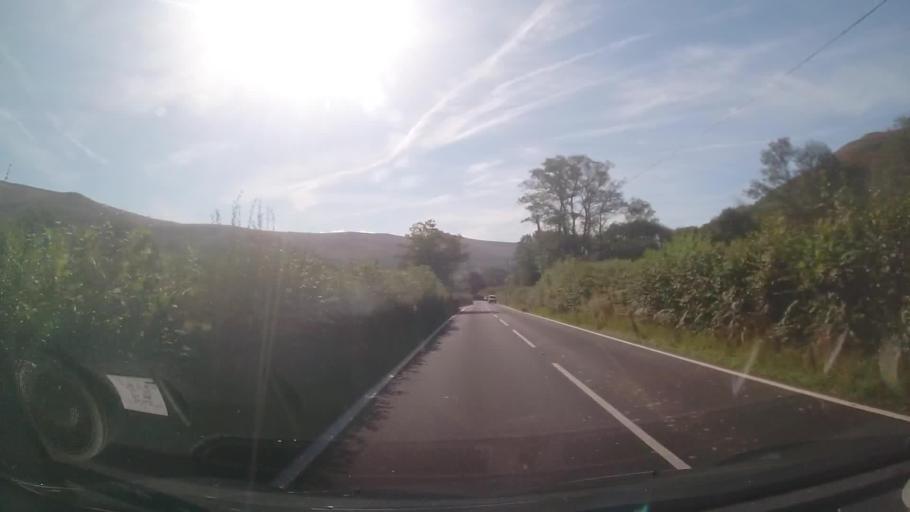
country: GB
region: Wales
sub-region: Sir Powys
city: Hay
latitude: 51.9497
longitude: -3.1918
